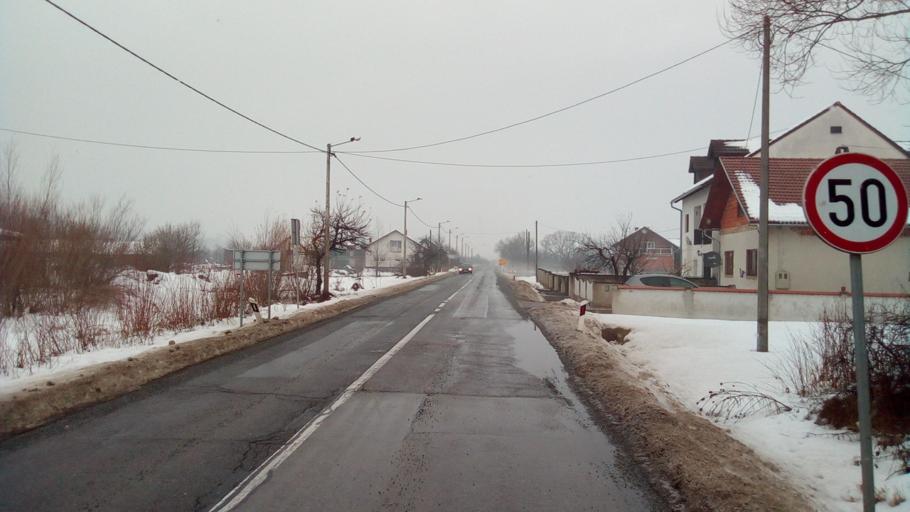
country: HR
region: Sisacko-Moslavacka
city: Petrinja
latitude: 45.4098
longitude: 16.2978
